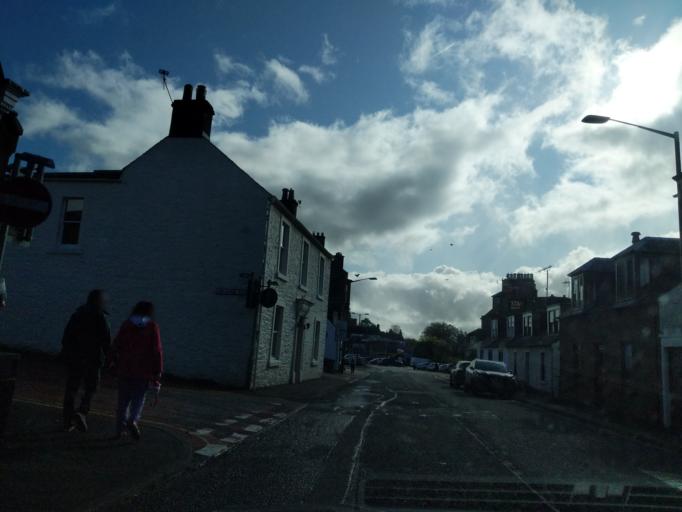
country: GB
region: Scotland
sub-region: Dumfries and Galloway
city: Moffat
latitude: 55.3350
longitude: -3.4455
